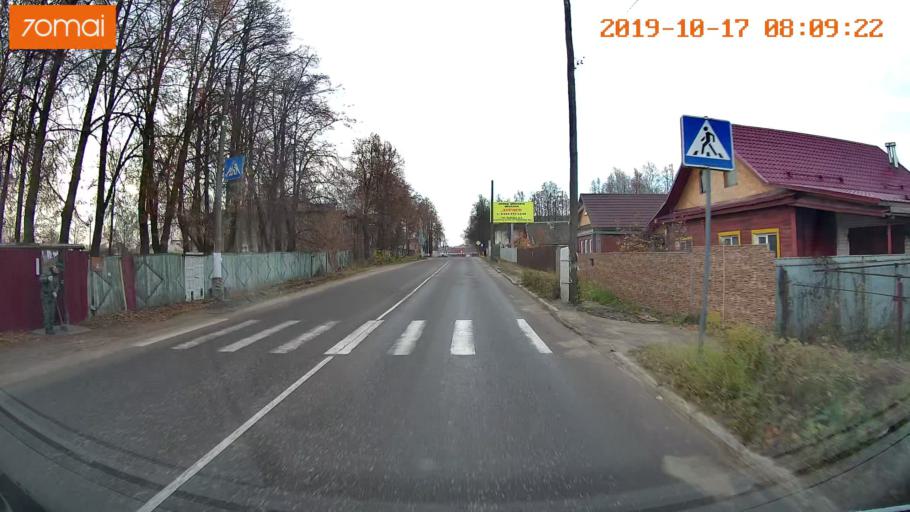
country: RU
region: Vladimir
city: Kol'chugino
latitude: 56.3125
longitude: 39.3808
